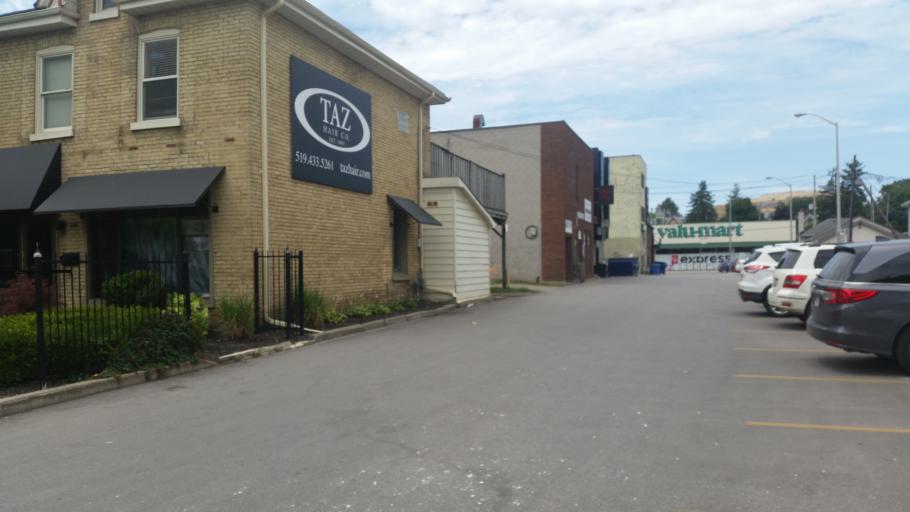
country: CA
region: Ontario
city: London
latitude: 42.9947
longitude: -81.2521
